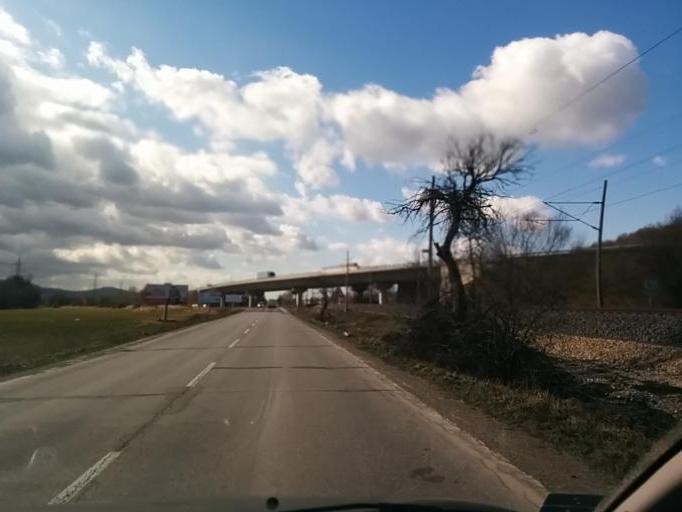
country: SK
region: Trenciansky
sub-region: Okres Trencin
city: Trencin
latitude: 48.8842
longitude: 17.9829
